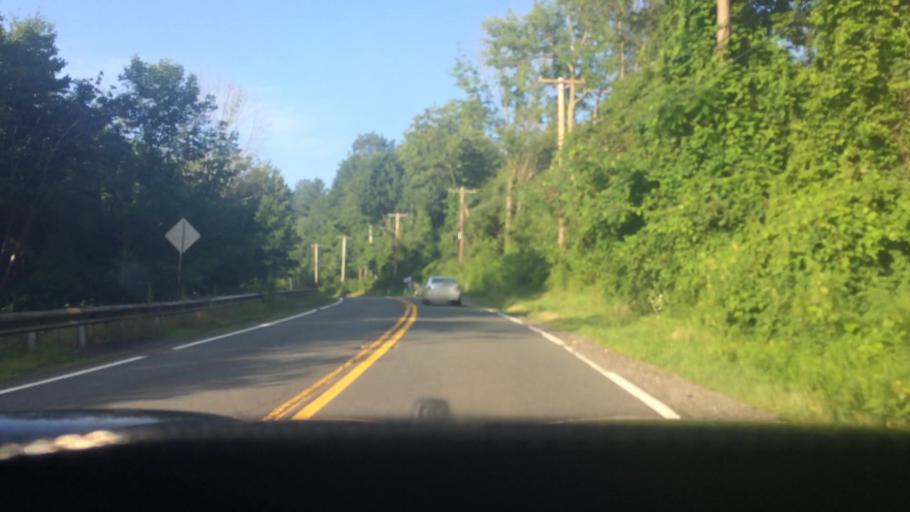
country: US
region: Massachusetts
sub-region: Franklin County
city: Erving
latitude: 42.5980
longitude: -72.4407
